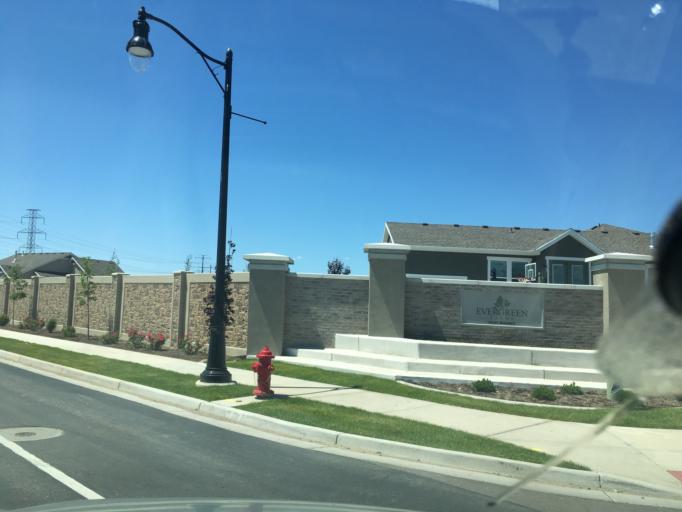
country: US
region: Utah
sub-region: Davis County
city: Layton
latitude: 41.0493
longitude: -111.9978
